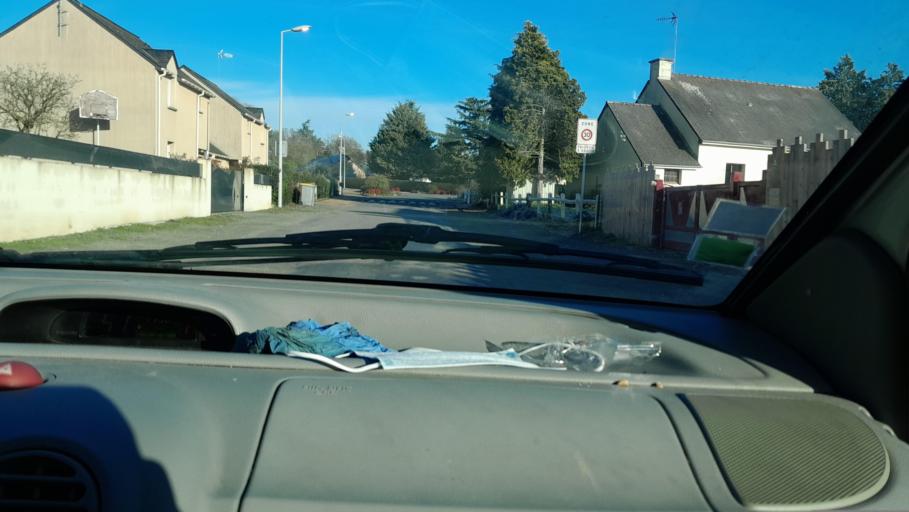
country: FR
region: Brittany
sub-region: Departement d'Ille-et-Vilaine
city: Rannee
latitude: 47.8839
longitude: -1.1803
